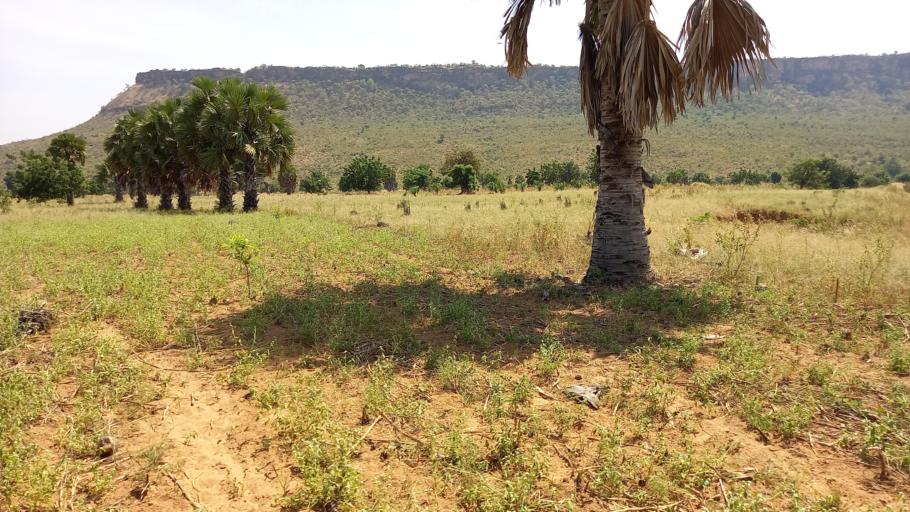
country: TG
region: Savanes
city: Dapaong
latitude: 10.8278
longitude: 0.3290
